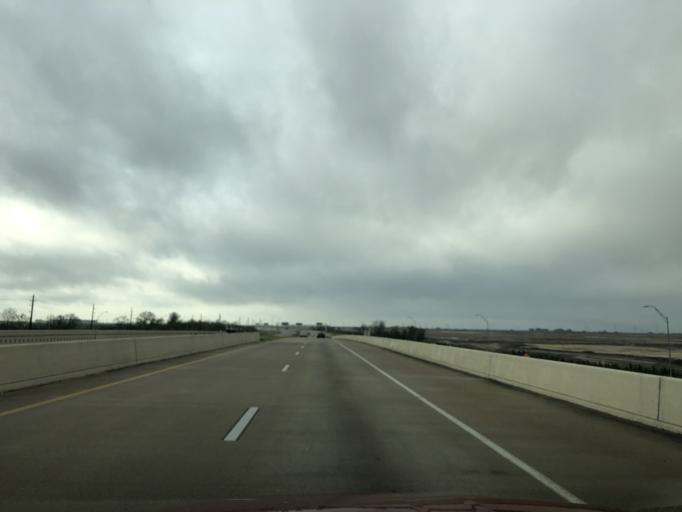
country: US
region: Texas
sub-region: Harris County
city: Cypress
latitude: 29.9537
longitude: -95.7698
